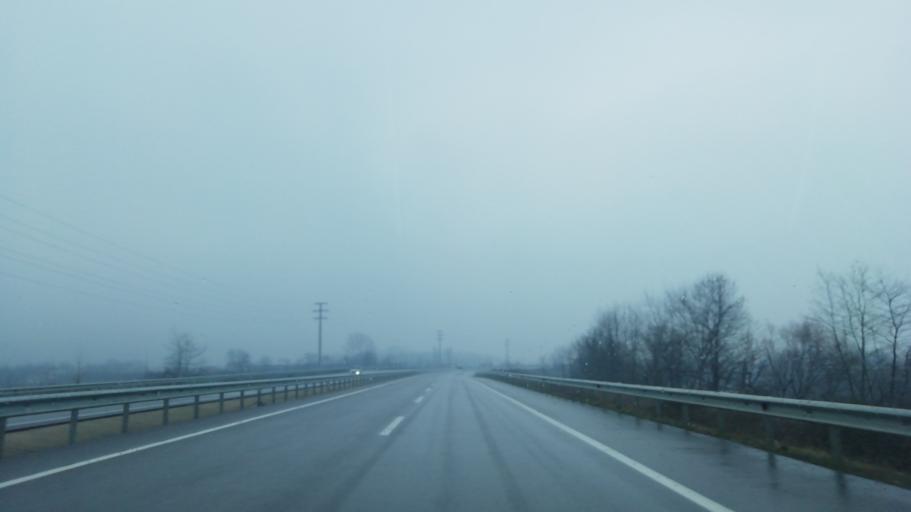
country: TR
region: Sakarya
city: Akyazi
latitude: 40.6472
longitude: 30.6087
